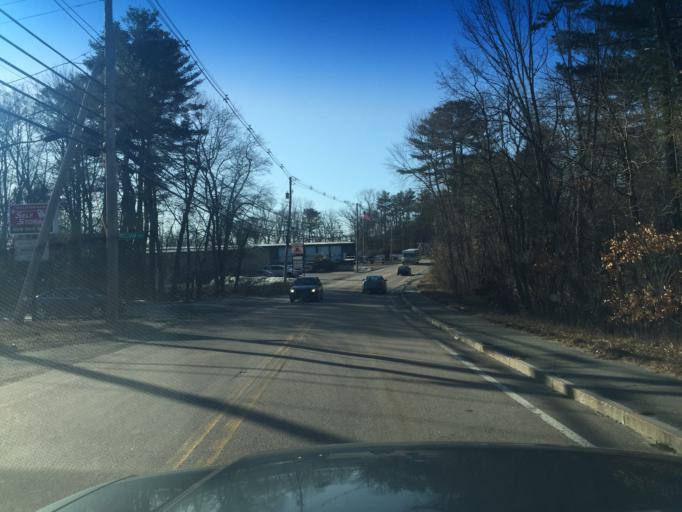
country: US
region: Massachusetts
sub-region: Norfolk County
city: Bellingham
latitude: 42.0876
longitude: -71.4960
